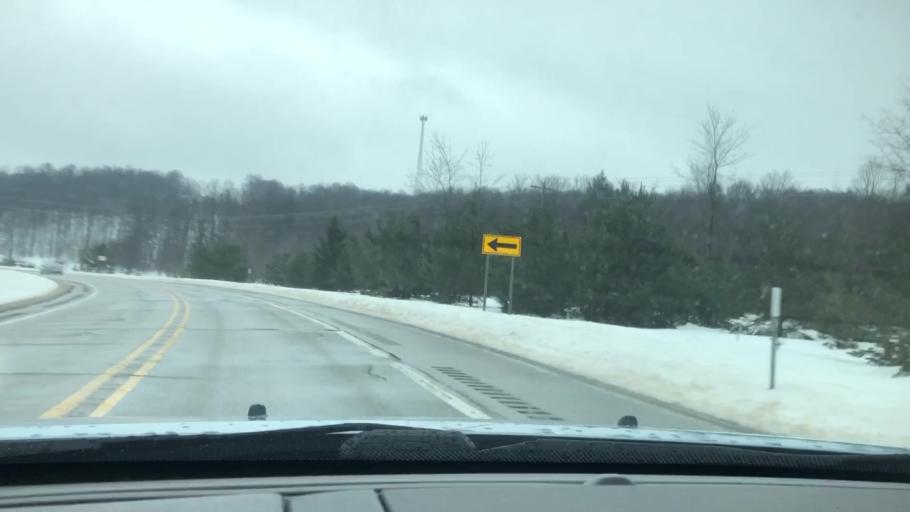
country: US
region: Michigan
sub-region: Charlevoix County
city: Boyne City
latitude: 45.0818
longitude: -84.9216
